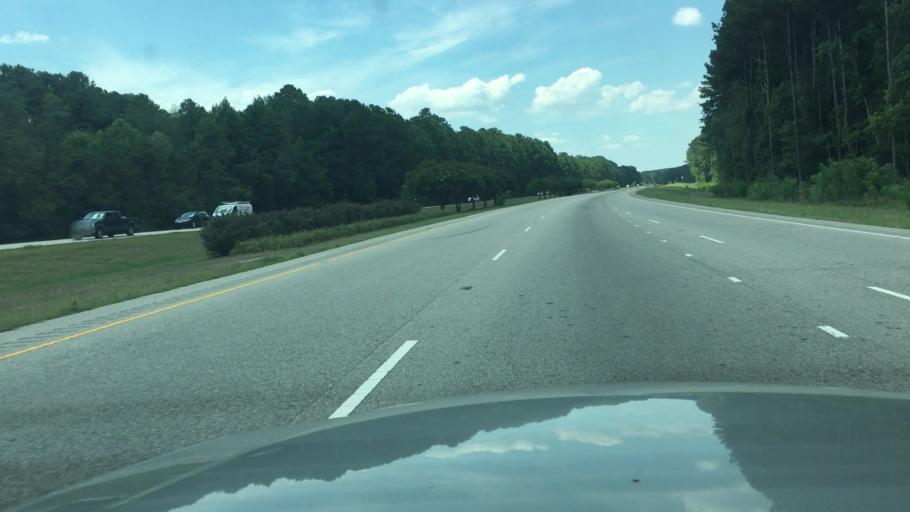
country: US
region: North Carolina
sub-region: Cumberland County
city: Fayetteville
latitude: 34.9829
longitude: -78.8598
